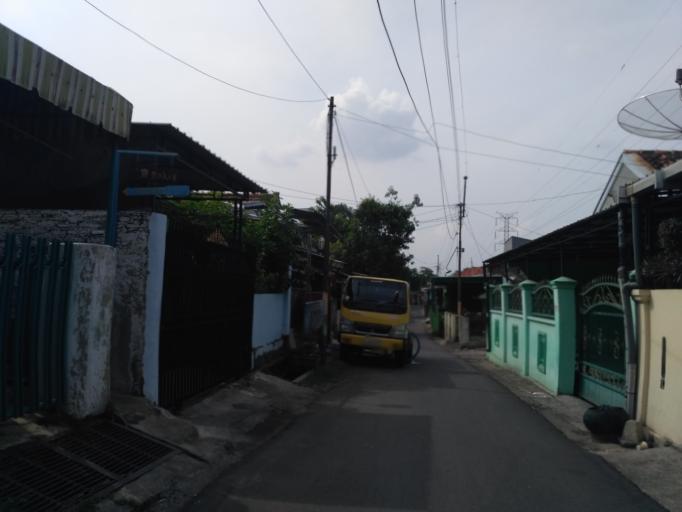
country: ID
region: Central Java
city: Semarang
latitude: -7.0187
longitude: 110.4434
